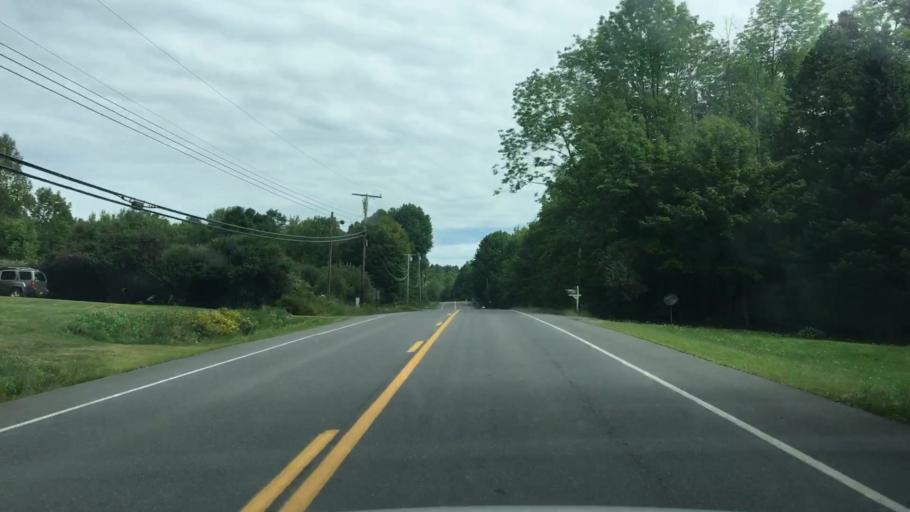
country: US
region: Maine
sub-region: Piscataquis County
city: Dover-Foxcroft
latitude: 45.2101
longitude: -69.1747
